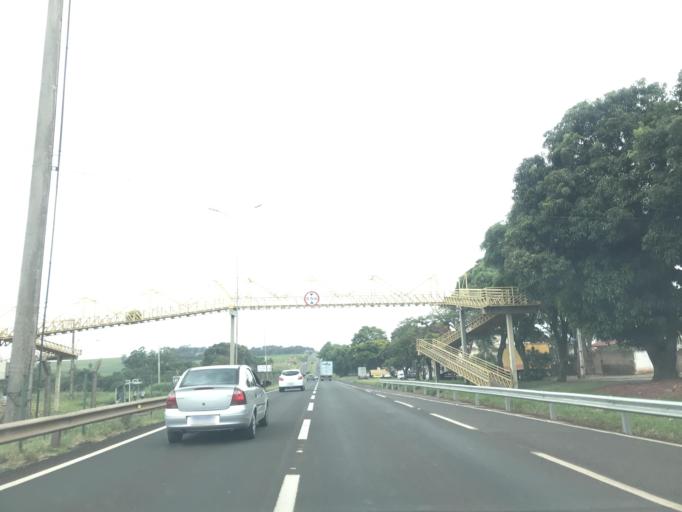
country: BR
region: Parana
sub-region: Mandaguacu
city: Mandaguacu
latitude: -23.3837
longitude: -52.0302
